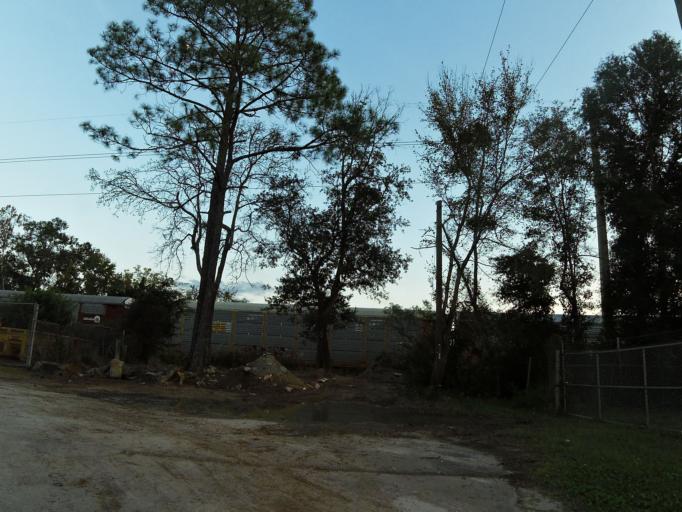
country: US
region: Florida
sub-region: Duval County
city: Jacksonville
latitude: 30.3553
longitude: -81.7344
